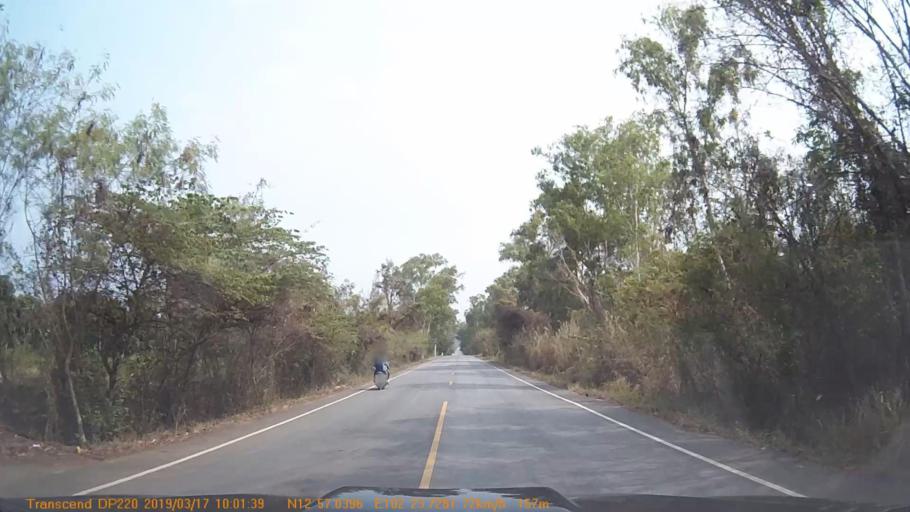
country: TH
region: Chanthaburi
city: Pong Nam Ron
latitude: 12.9528
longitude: 102.3956
